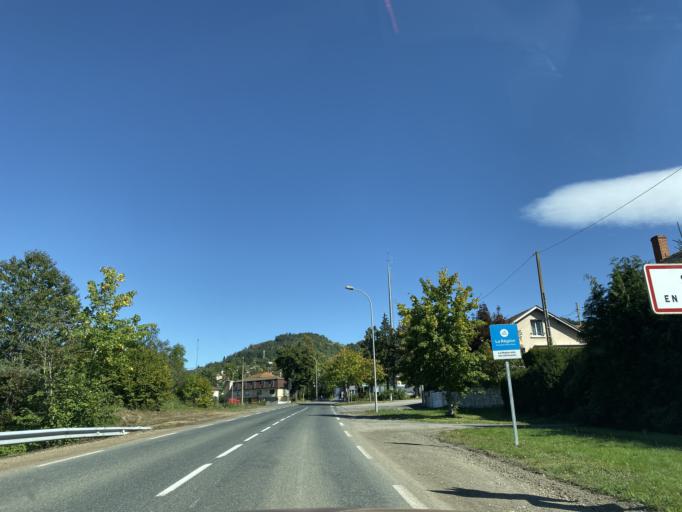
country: FR
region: Rhone-Alpes
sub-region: Departement de la Loire
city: Saint-Just-en-Chevalet
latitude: 45.9082
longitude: 3.8428
